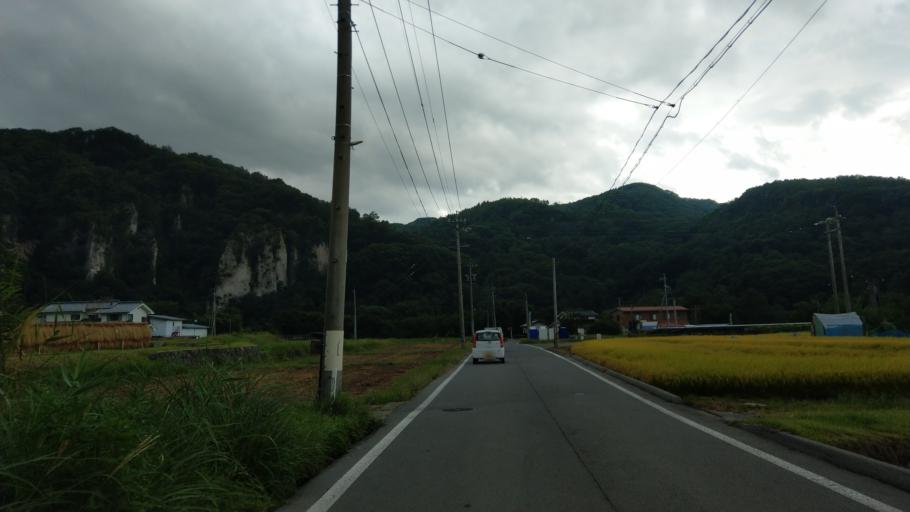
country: JP
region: Nagano
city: Komoro
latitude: 36.3285
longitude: 138.4072
